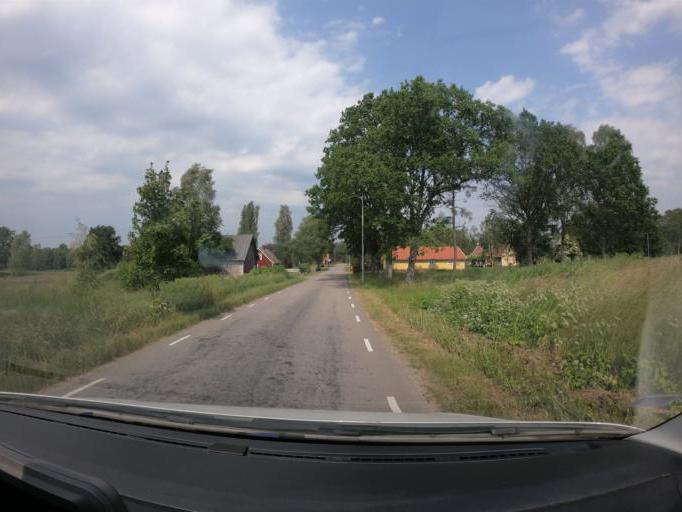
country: SE
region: Skane
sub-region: Hassleholms Kommun
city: Bjarnum
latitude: 56.3124
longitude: 13.5877
